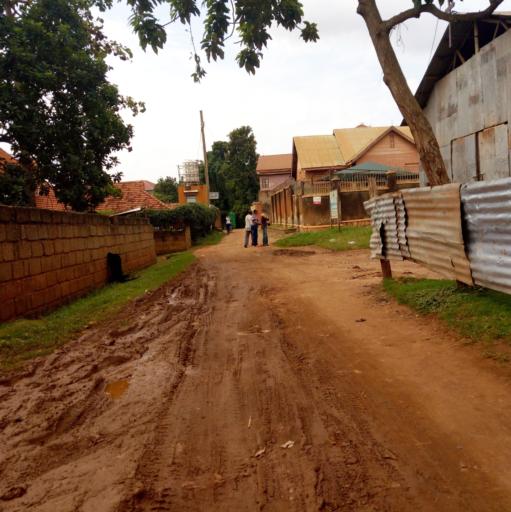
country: UG
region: Central Region
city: Kampala Central Division
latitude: 0.3444
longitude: 32.5598
